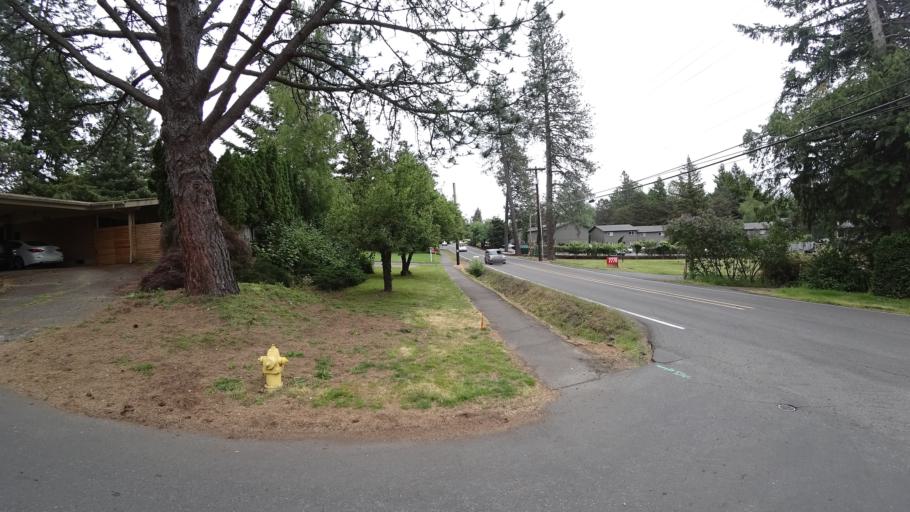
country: US
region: Oregon
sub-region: Washington County
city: Garden Home-Whitford
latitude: 45.4658
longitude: -122.7578
